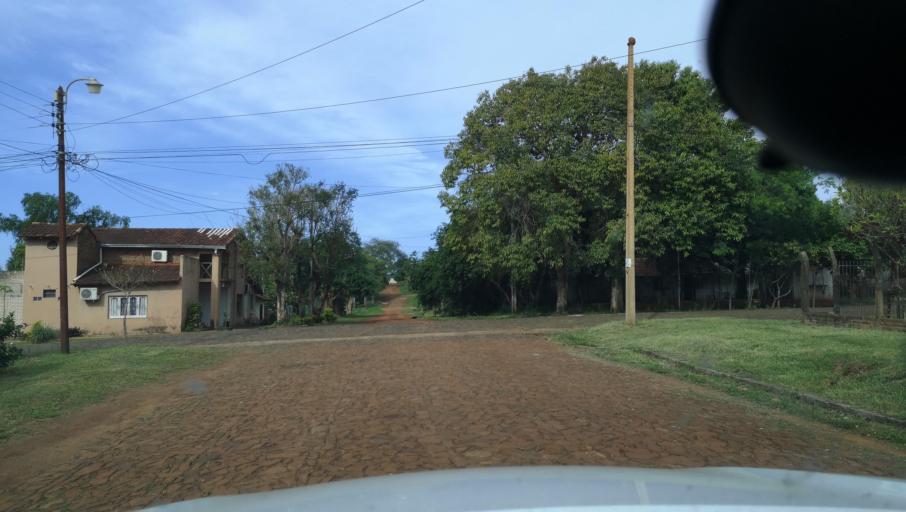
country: PY
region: Itapua
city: Carmen del Parana
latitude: -27.1620
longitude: -56.2343
